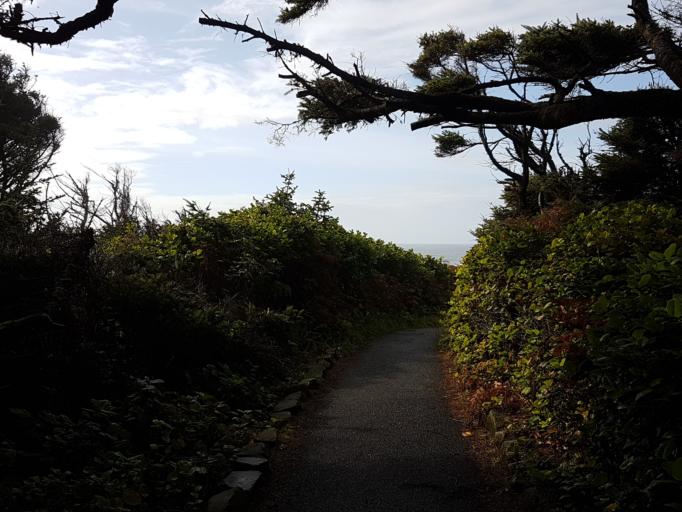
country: US
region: Oregon
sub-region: Lincoln County
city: Waldport
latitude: 44.2837
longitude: -124.1108
